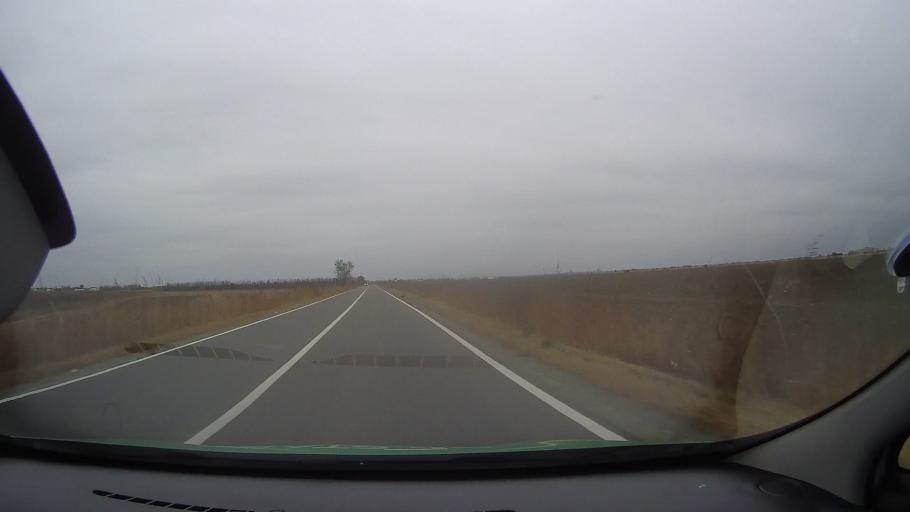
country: RO
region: Ialomita
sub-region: Comuna Slobozia
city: Slobozia
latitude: 44.6161
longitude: 27.3868
